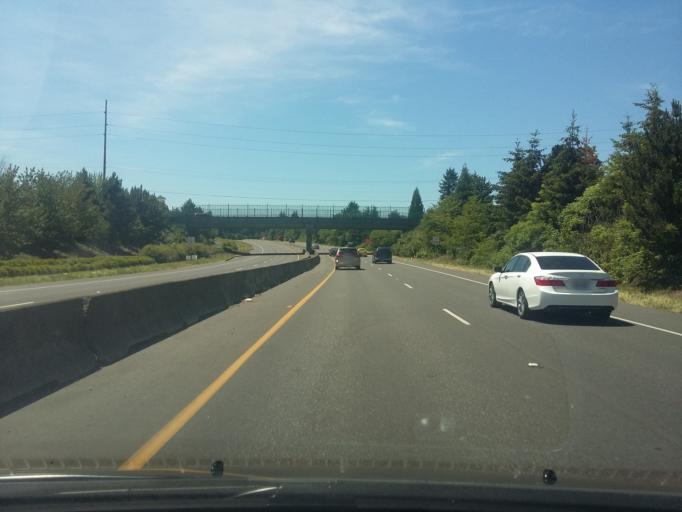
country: US
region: Washington
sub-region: Clark County
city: Five Corners
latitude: 45.6823
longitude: -122.5615
